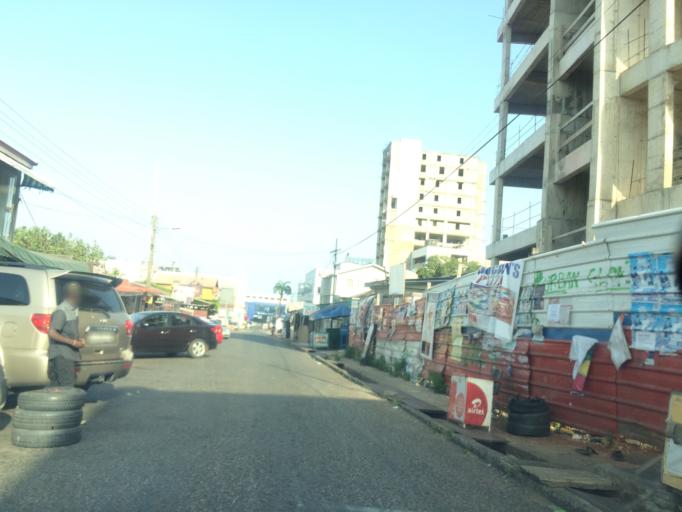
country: GH
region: Greater Accra
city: Accra
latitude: 5.5611
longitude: -0.1841
